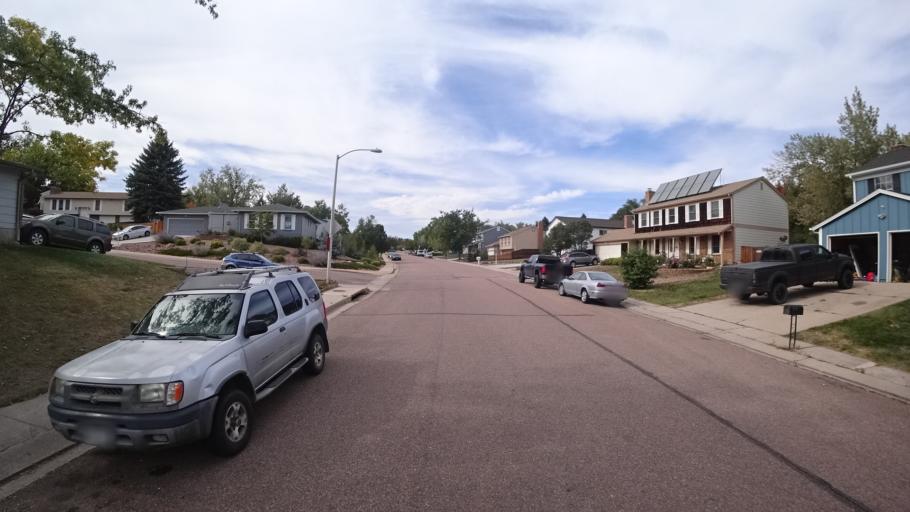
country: US
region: Colorado
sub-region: El Paso County
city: Colorado Springs
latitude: 38.9032
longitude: -104.7812
